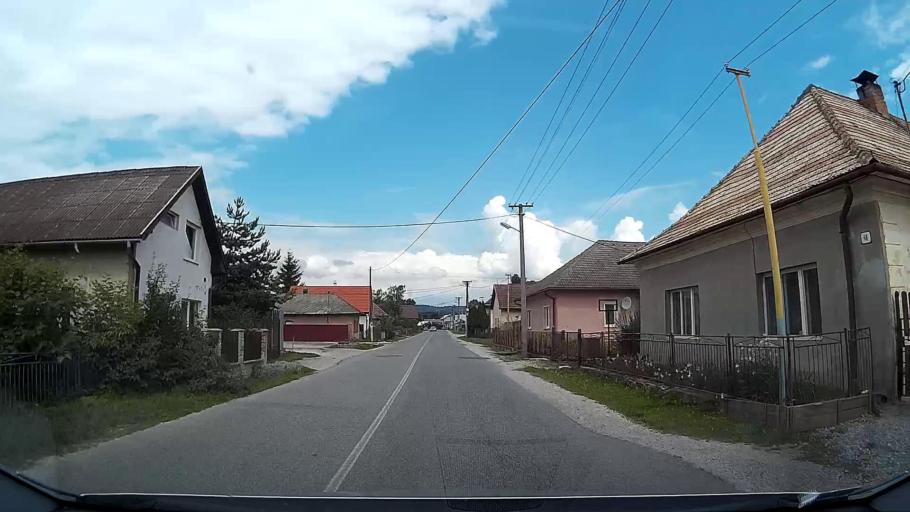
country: SK
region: Presovsky
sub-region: Okres Poprad
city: Poprad
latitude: 48.9785
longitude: 20.3917
